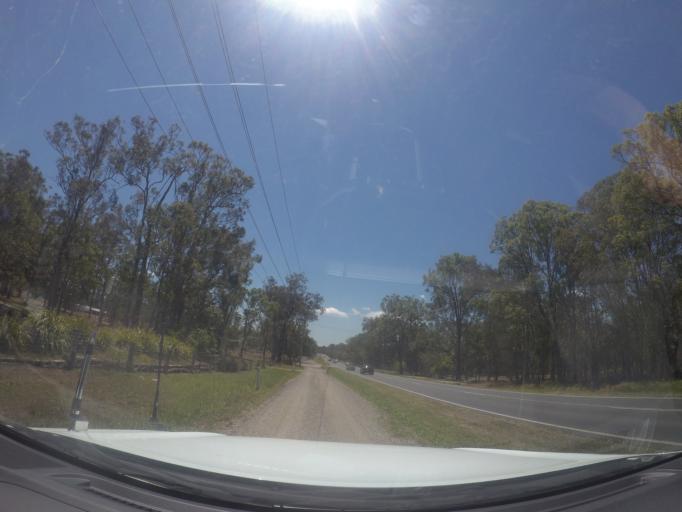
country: AU
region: Queensland
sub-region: Logan
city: Logan Reserve
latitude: -27.7398
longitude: 153.1274
